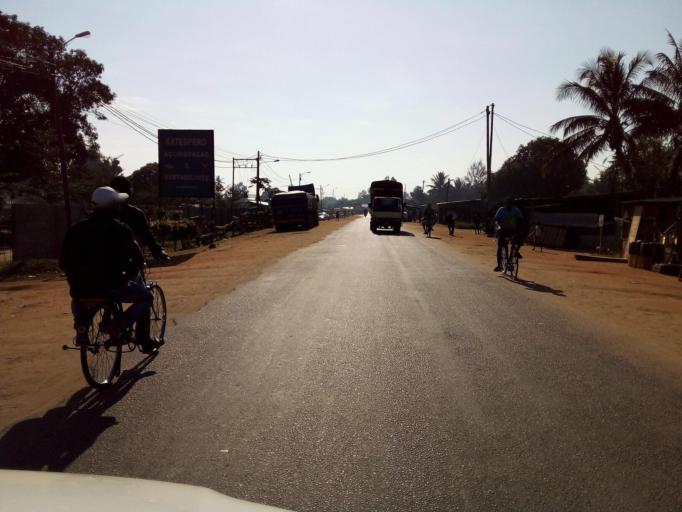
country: MZ
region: Zambezia
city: Quelimane
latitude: -17.5966
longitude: 36.8117
